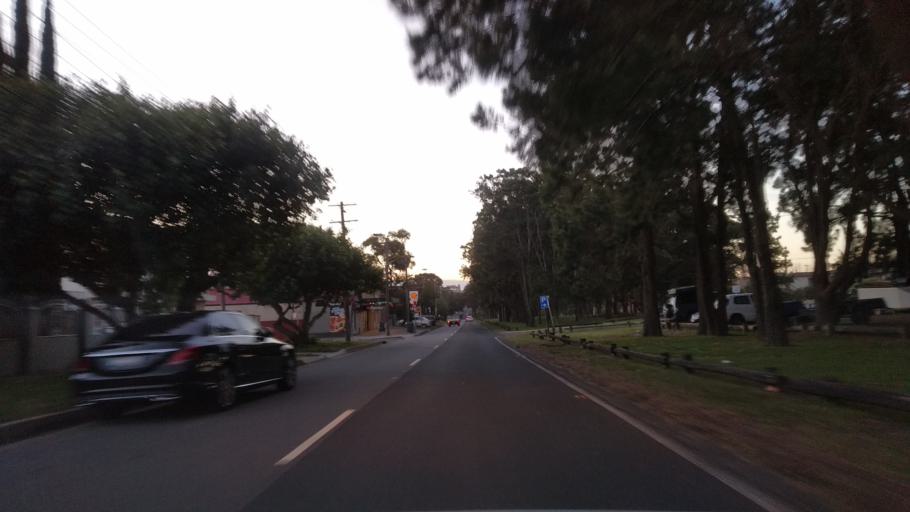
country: AU
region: New South Wales
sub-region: Randwick
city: Maroubra
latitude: -33.9512
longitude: 151.2414
